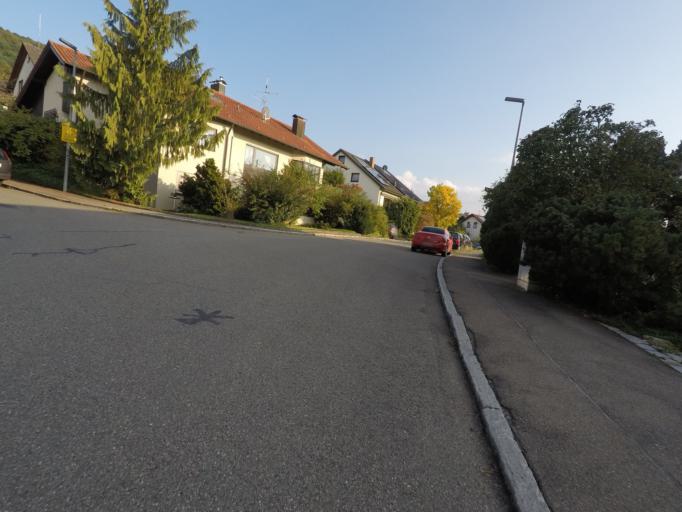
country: DE
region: Baden-Wuerttemberg
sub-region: Tuebingen Region
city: Pfullingen
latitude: 48.4652
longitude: 9.2380
